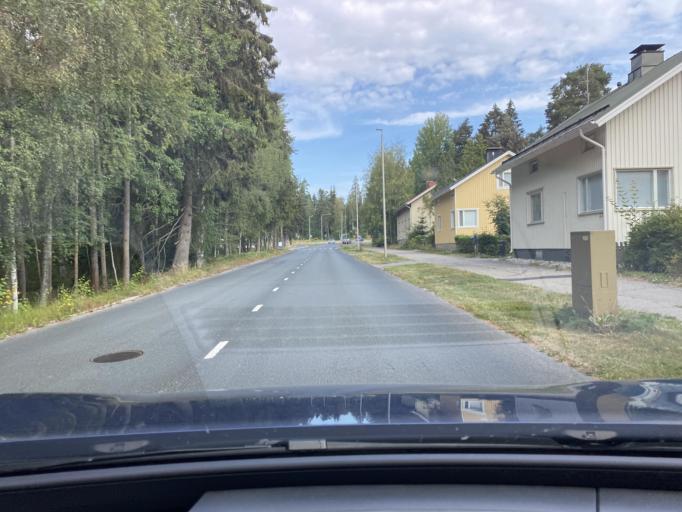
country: FI
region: Pirkanmaa
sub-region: Lounais-Pirkanmaa
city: Vammala
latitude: 61.3537
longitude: 22.8936
